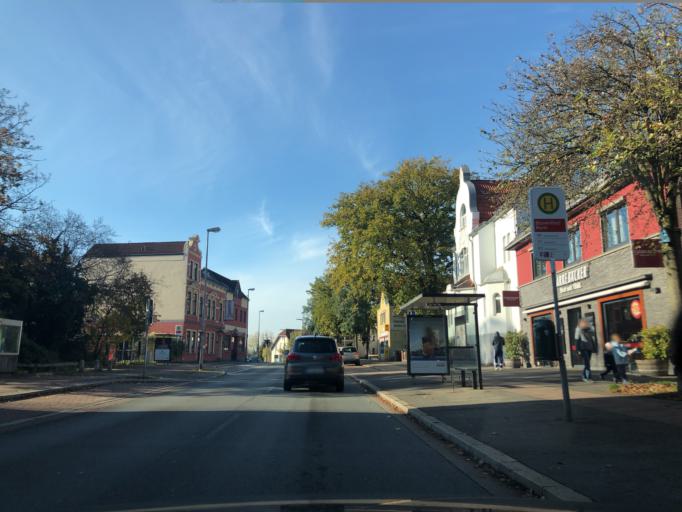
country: DE
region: Lower Saxony
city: Lemwerder
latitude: 53.1815
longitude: 8.5743
